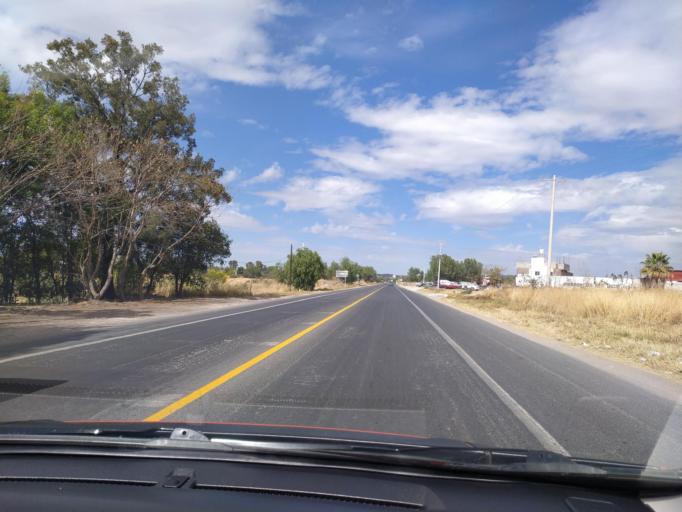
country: LA
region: Oudomxai
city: Muang La
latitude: 21.0159
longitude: 101.8275
